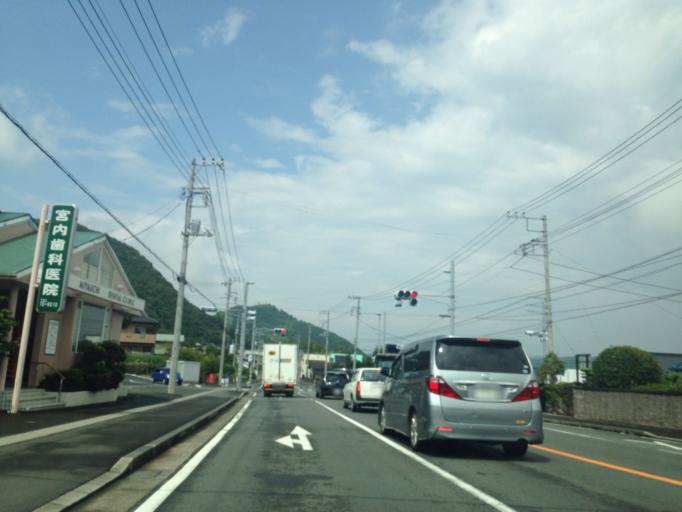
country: JP
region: Shizuoka
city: Ito
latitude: 34.9596
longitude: 138.9372
